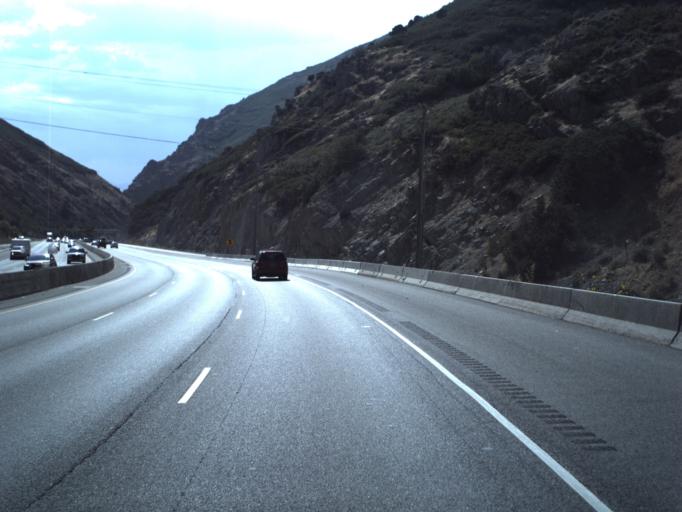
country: US
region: Utah
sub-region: Salt Lake County
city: Mount Olympus
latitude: 40.7250
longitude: -111.7717
